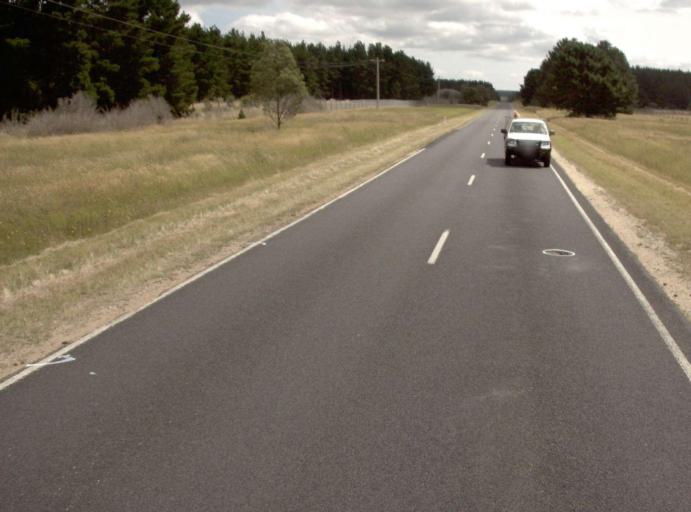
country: AU
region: Victoria
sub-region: Wellington
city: Sale
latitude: -38.1670
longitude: 147.0388
